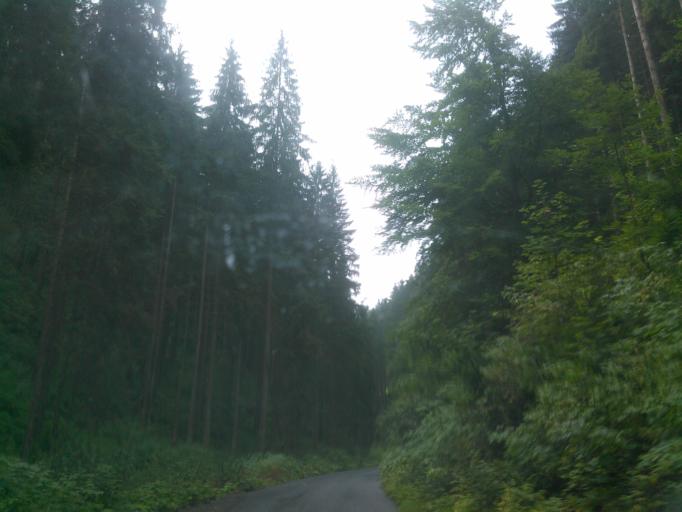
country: SK
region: Zilinsky
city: Ruzomberok
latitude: 48.9658
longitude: 19.4084
